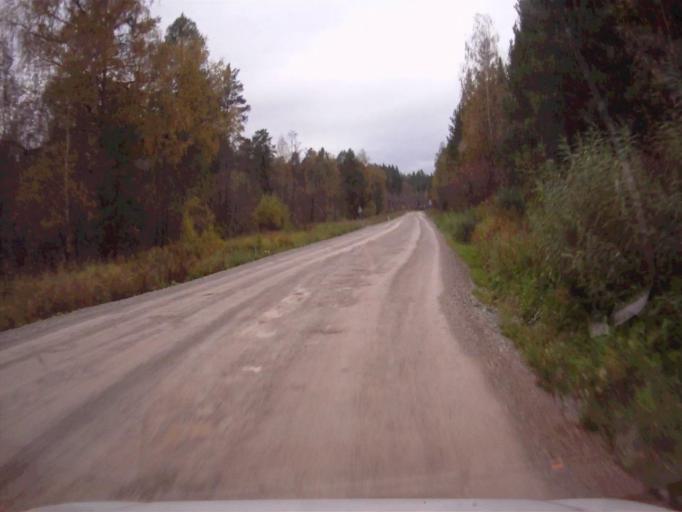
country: RU
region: Chelyabinsk
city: Nyazepetrovsk
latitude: 56.0436
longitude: 59.5062
